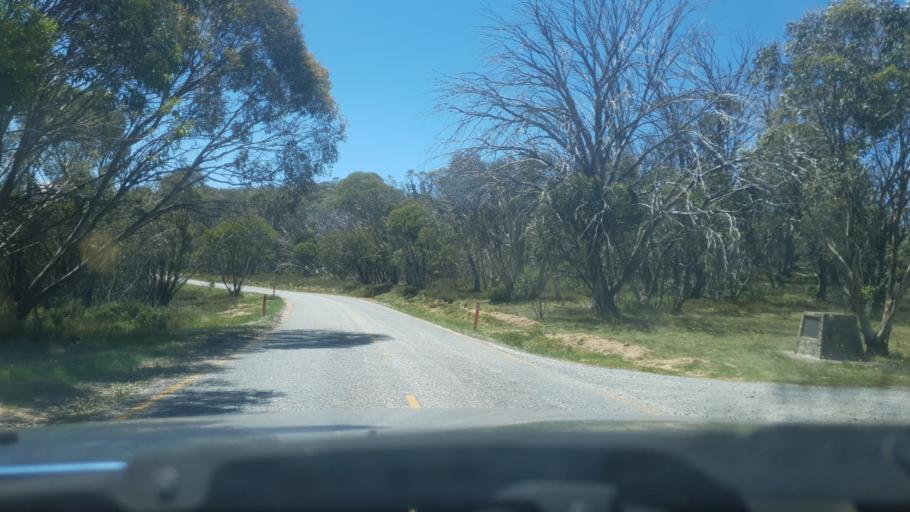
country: AU
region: Victoria
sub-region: Alpine
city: Mount Beauty
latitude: -36.9421
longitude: 147.3181
